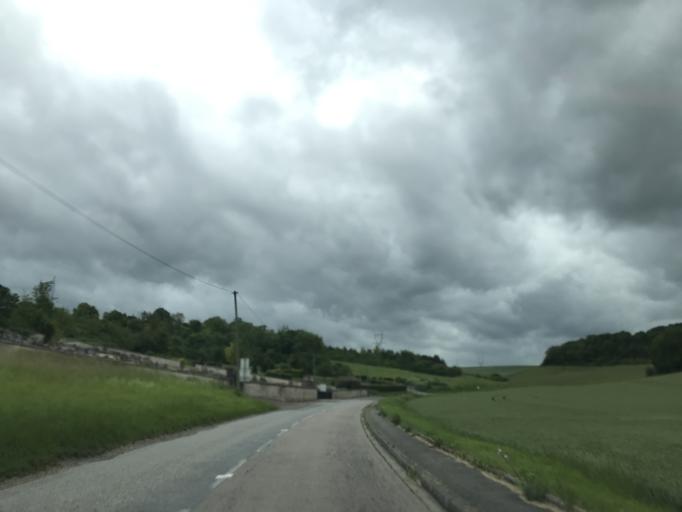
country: FR
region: Haute-Normandie
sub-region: Departement de l'Eure
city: Garennes-sur-Eure
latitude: 48.9052
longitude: 1.4333
